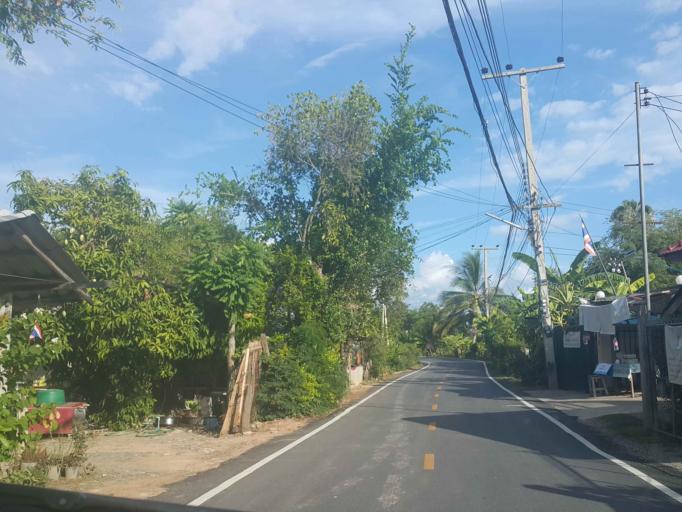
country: TH
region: Chiang Mai
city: San Sai
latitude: 18.8041
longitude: 99.0661
